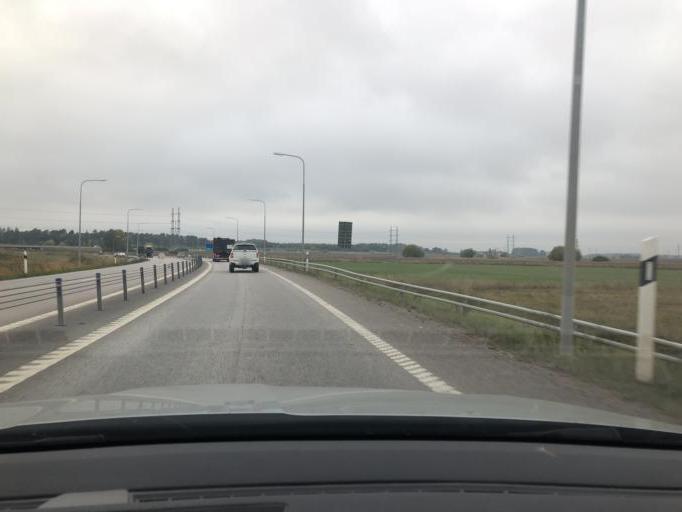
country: SE
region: Uppsala
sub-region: Uppsala Kommun
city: Gamla Uppsala
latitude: 59.8899
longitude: 17.6789
